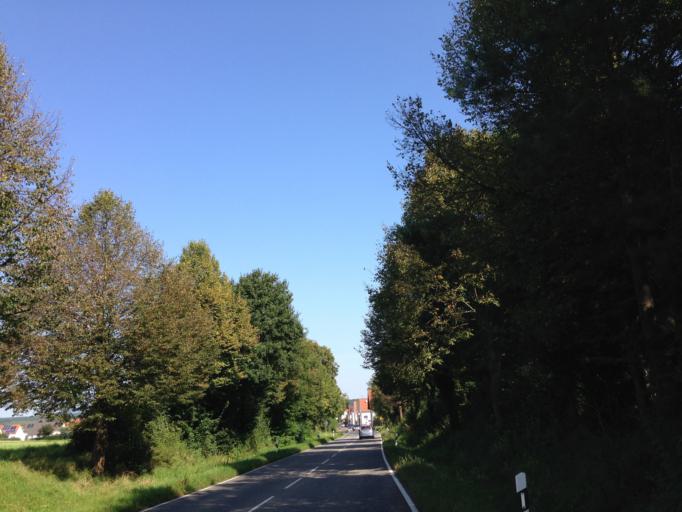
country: DE
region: Hesse
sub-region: Regierungsbezirk Giessen
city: Langgons
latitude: 50.5217
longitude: 8.6752
